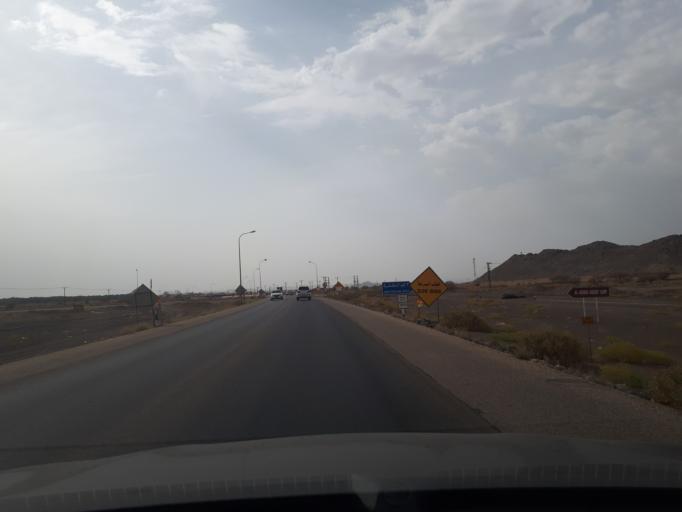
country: OM
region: Ash Sharqiyah
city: Al Qabil
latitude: 22.5604
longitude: 58.7105
